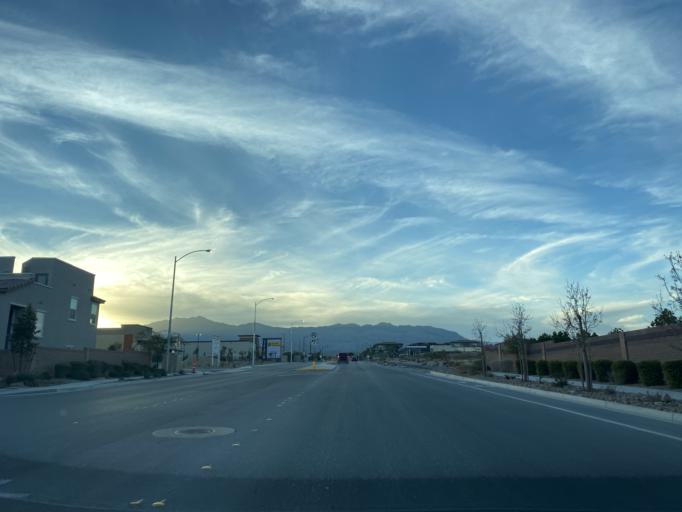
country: US
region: Nevada
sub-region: Clark County
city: Summerlin South
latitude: 36.2847
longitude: -115.3110
